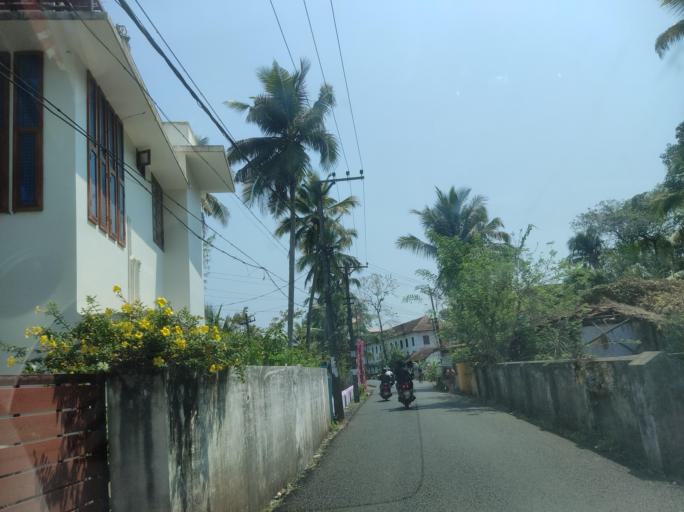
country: IN
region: Kerala
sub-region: Alappuzha
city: Kutiatodu
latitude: 9.7719
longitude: 76.3060
